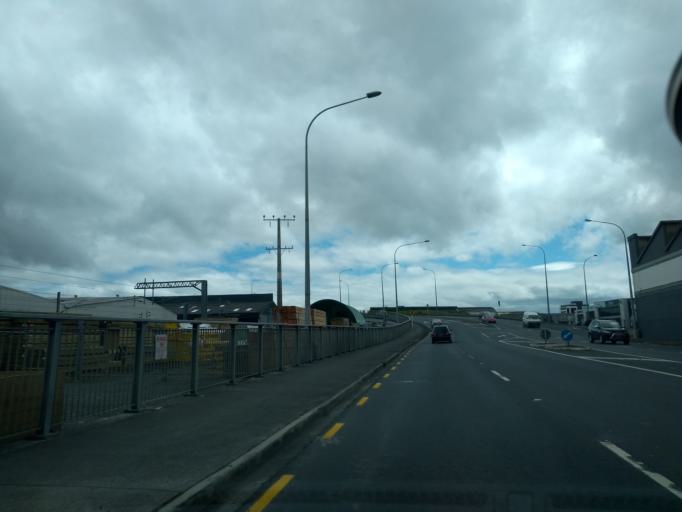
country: NZ
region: Auckland
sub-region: Auckland
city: Tamaki
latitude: -36.9088
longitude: 174.8153
